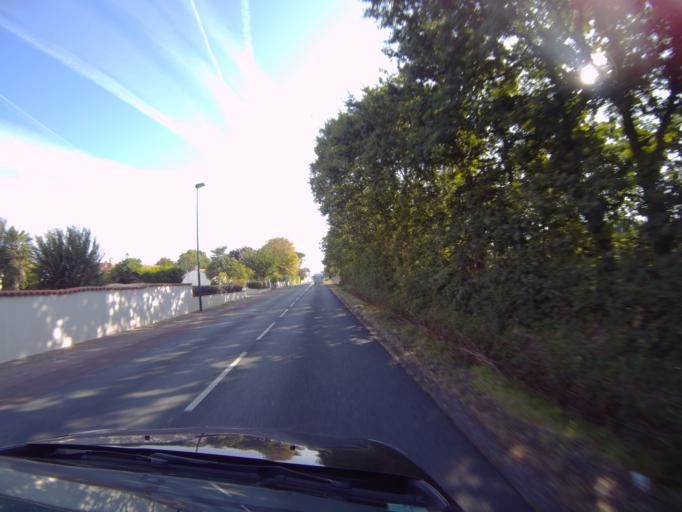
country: FR
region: Pays de la Loire
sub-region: Departement de la Vendee
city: Saint-Hilaire-de-Talmont
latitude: 46.5039
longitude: -1.5740
